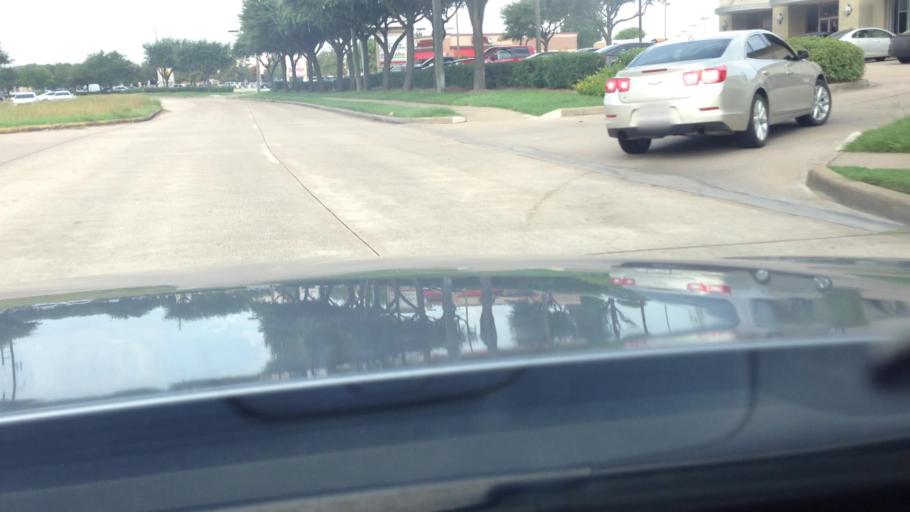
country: US
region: Texas
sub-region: Harris County
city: Hudson
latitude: 29.9559
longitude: -95.5440
